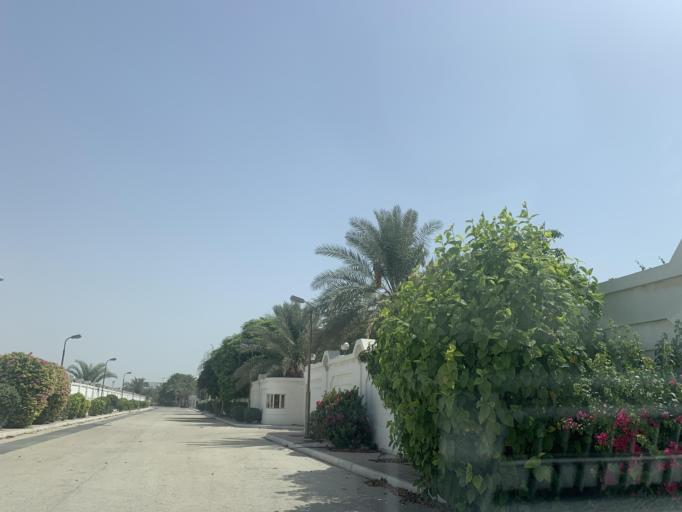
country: BH
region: Central Governorate
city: Madinat Hamad
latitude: 26.1470
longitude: 50.4928
